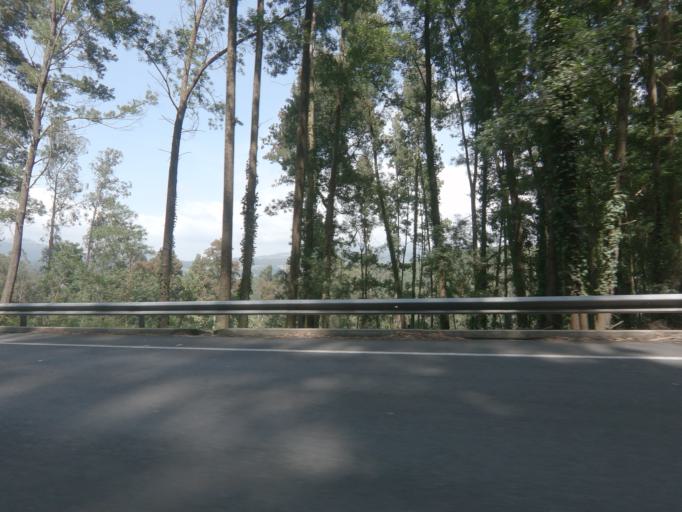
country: ES
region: Galicia
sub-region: Provincia de Pontevedra
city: Gondomar
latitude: 42.0925
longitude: -8.7543
